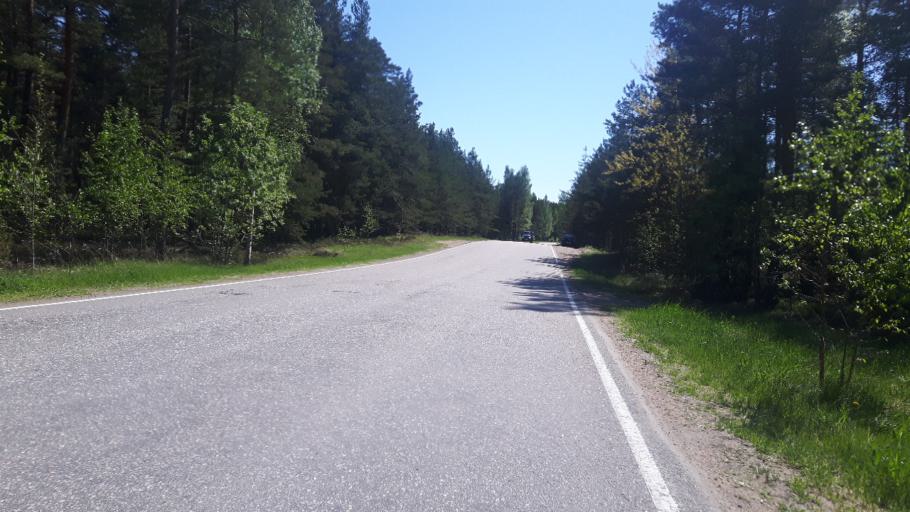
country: RU
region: Leningrad
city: Glebychevo
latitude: 60.3326
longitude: 28.8211
